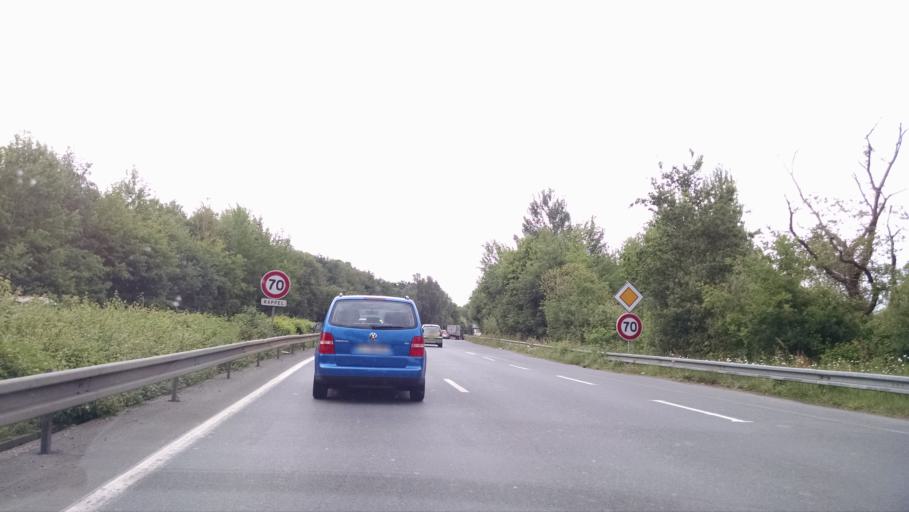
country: FR
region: Pays de la Loire
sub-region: Departement de la Loire-Atlantique
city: La Chapelle-sur-Erdre
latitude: 47.2632
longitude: -1.5580
